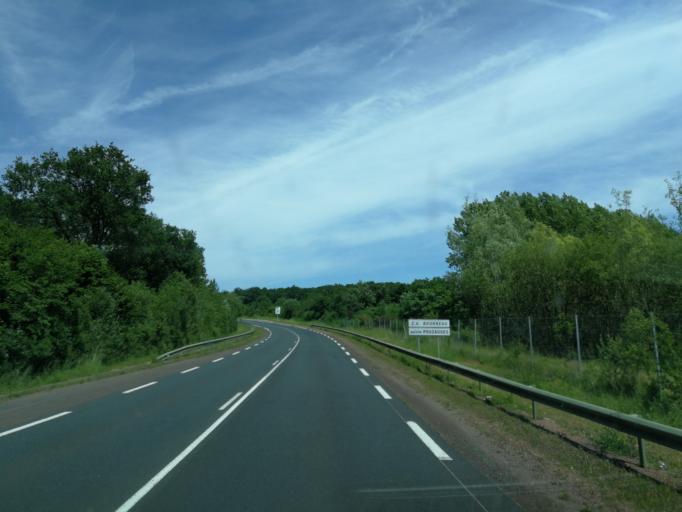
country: FR
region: Pays de la Loire
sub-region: Departement de la Vendee
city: Pissotte
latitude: 46.5126
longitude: -0.8101
